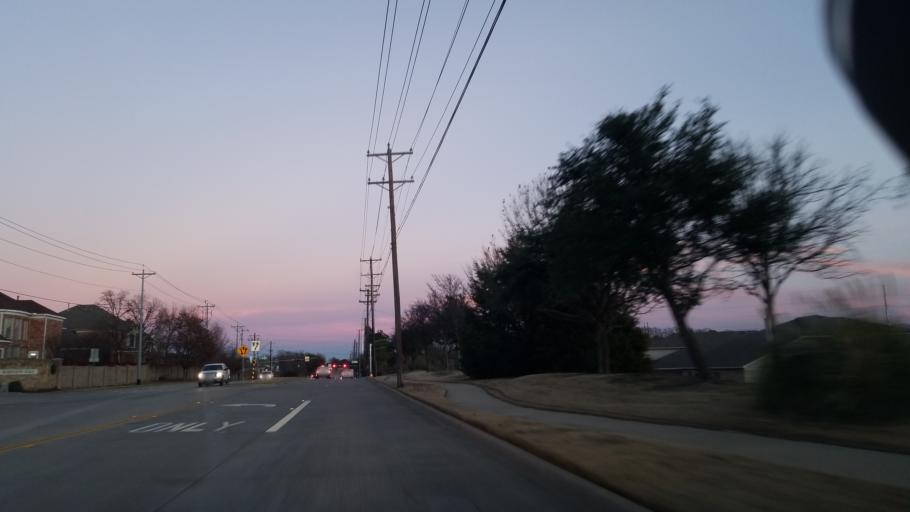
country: US
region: Texas
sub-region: Denton County
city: Corinth
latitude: 33.1582
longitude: -97.0955
